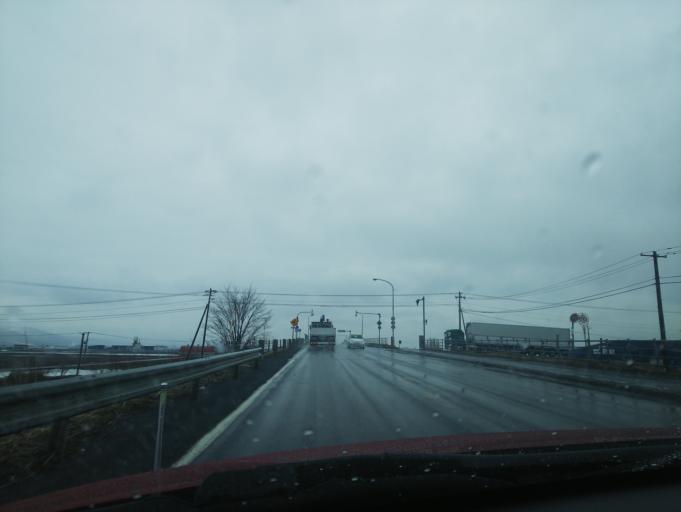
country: JP
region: Hokkaido
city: Nayoro
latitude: 44.1952
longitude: 142.3949
